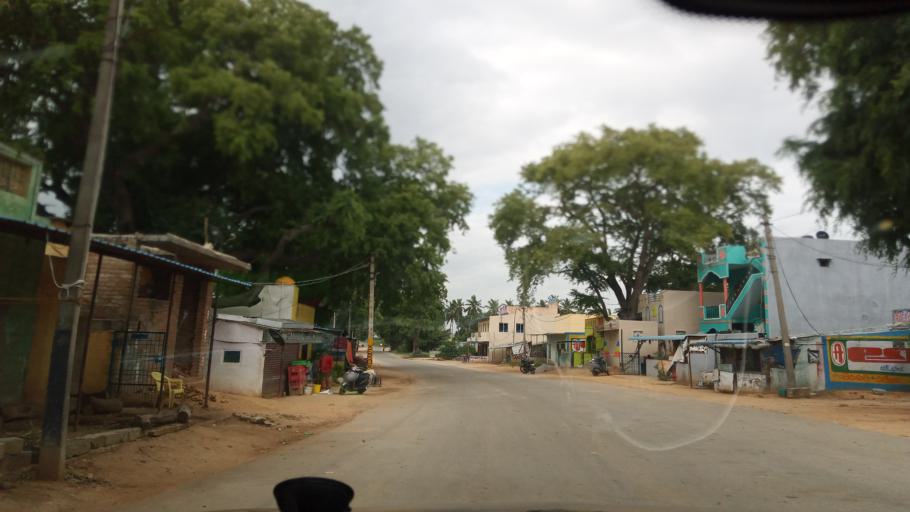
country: IN
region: Andhra Pradesh
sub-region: Chittoor
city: Palmaner
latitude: 13.1851
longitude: 78.8376
